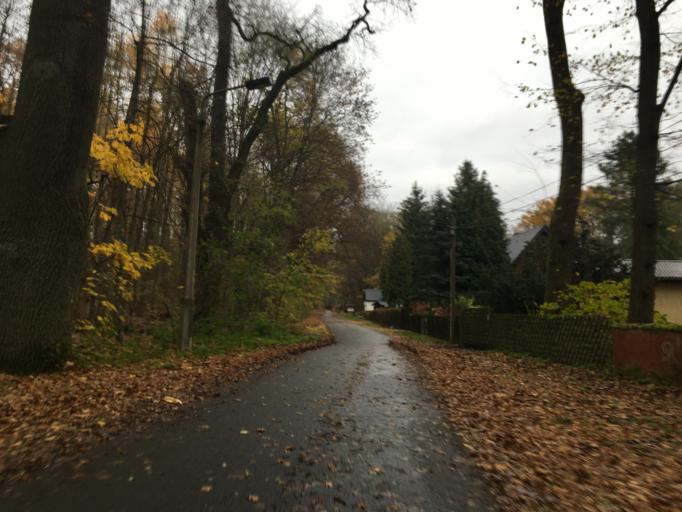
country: DE
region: Brandenburg
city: Gross Lindow
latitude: 52.2841
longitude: 14.5136
